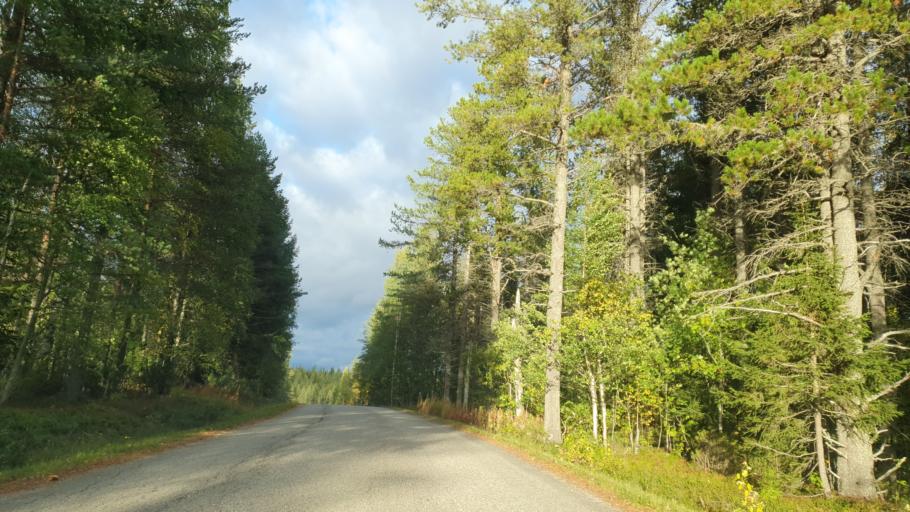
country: FI
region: North Karelia
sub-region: Pielisen Karjala
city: Lieksa
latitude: 63.9188
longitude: 30.1298
